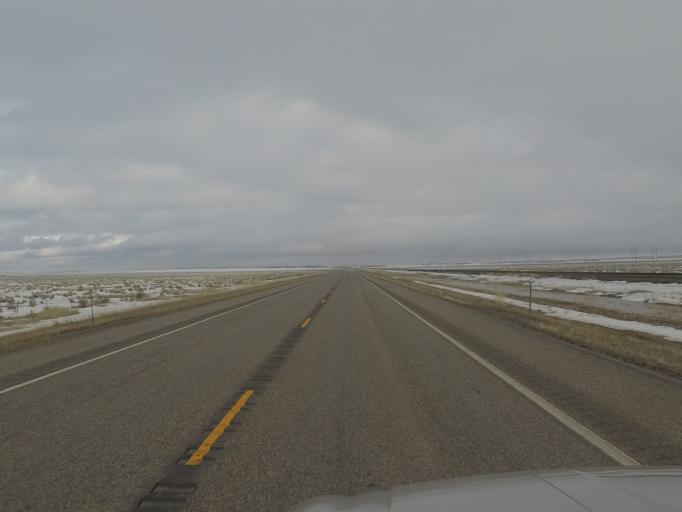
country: US
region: Montana
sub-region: Yellowstone County
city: Billings
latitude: 45.9684
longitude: -108.7372
